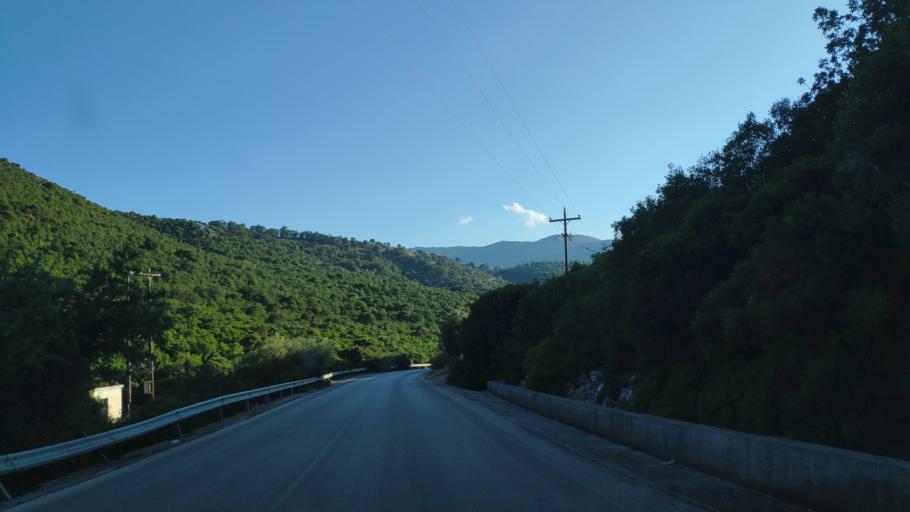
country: GR
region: West Greece
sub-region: Nomos Aitolias kai Akarnanias
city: Astakos
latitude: 38.6007
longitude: 21.1107
